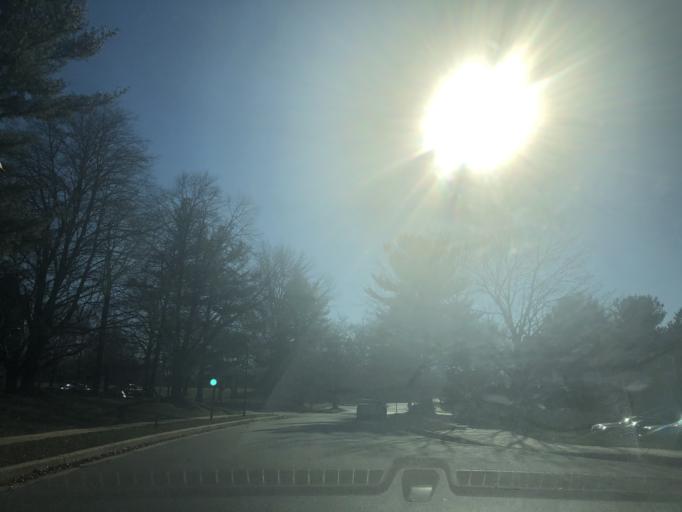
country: US
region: Maryland
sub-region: Howard County
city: Riverside
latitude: 39.1922
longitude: -76.8466
